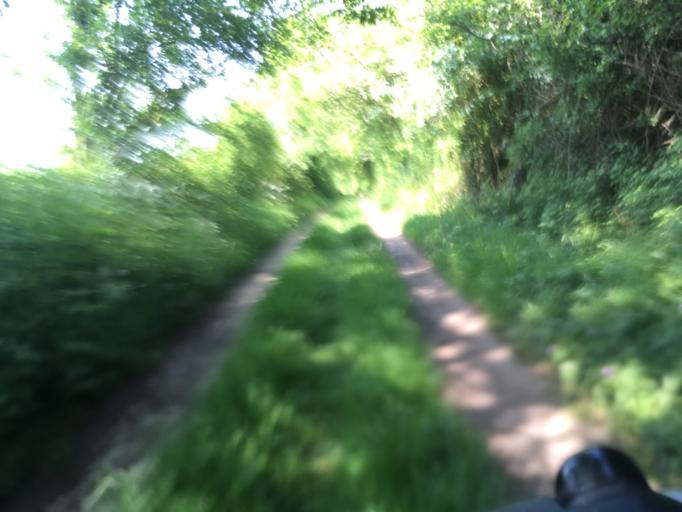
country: GB
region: England
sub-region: South Gloucestershire
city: Falfield
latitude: 51.6189
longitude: -2.4518
